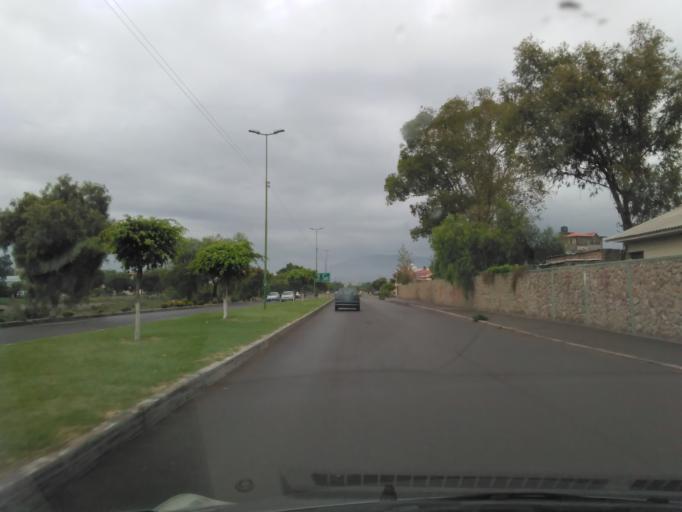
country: BO
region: Cochabamba
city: Cochabamba
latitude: -17.3989
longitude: -66.1686
